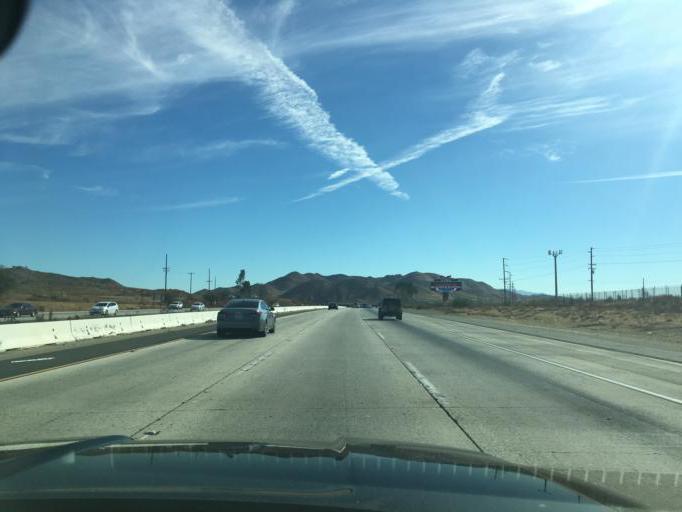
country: US
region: California
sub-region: Riverside County
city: Lake Elsinore
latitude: 33.6724
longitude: -117.3142
